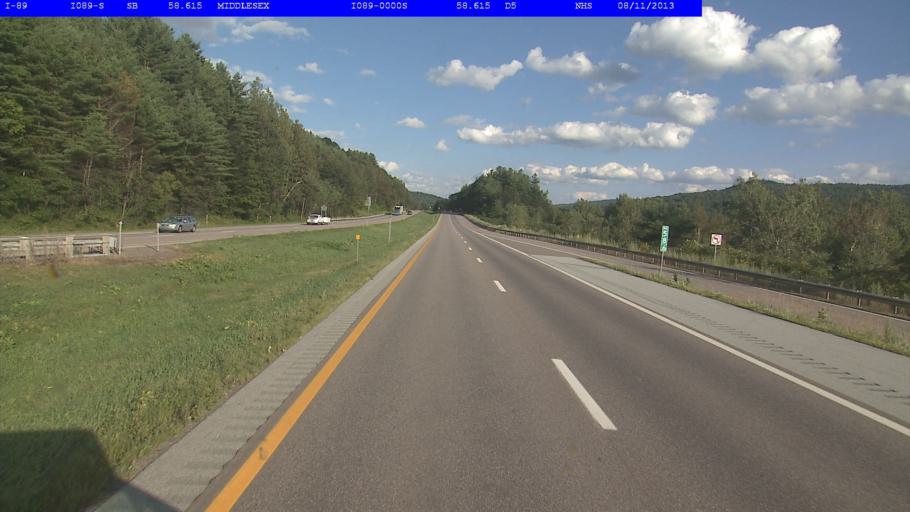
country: US
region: Vermont
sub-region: Washington County
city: Waterbury
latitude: 44.2971
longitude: -72.6839
